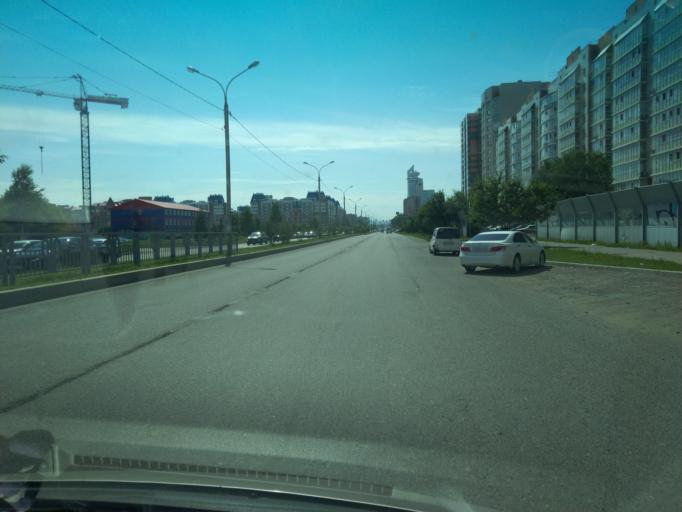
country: RU
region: Krasnoyarskiy
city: Krasnoyarsk
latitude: 56.0495
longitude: 92.9207
